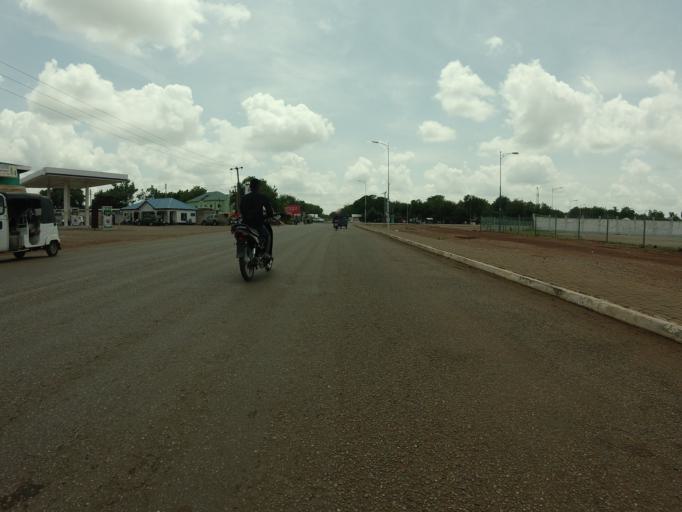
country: GH
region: Northern
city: Tamale
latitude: 9.4090
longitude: -0.8629
